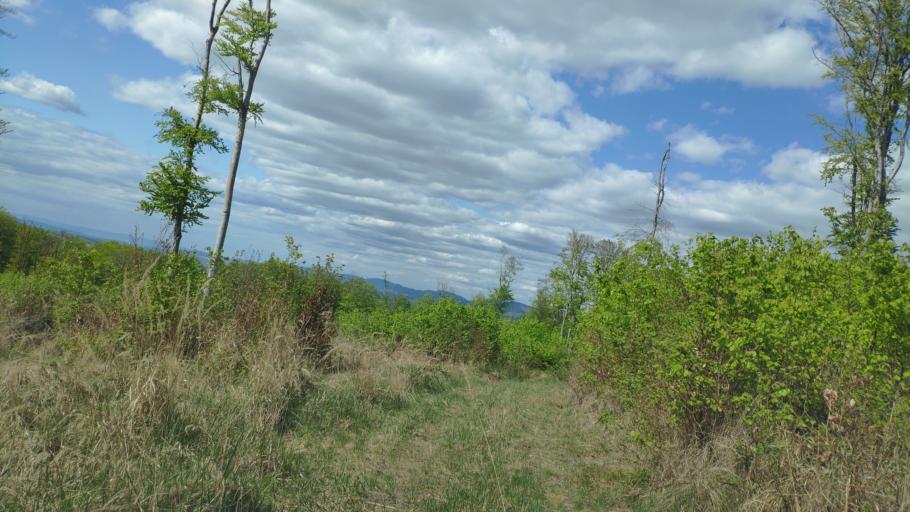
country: SK
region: Kosicky
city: Kosice
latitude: 48.6644
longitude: 21.4501
